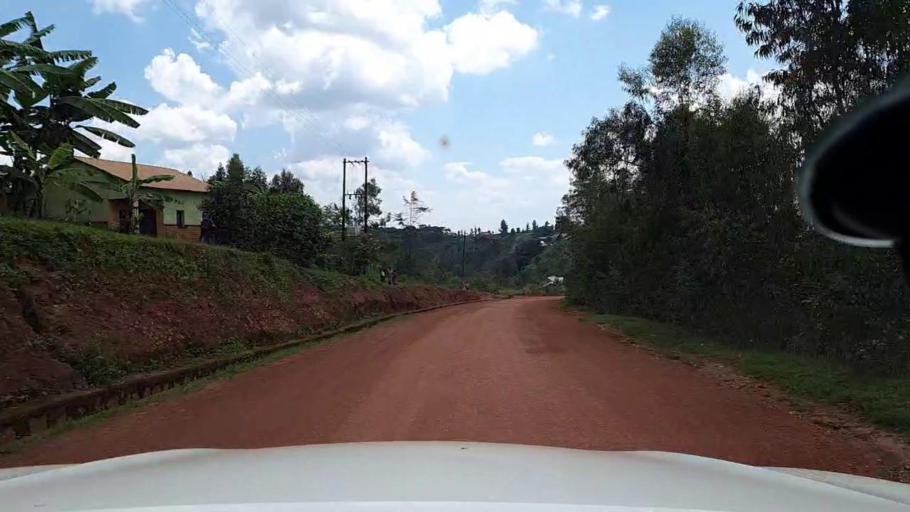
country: RW
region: Kigali
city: Kigali
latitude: -1.8007
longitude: 29.8433
